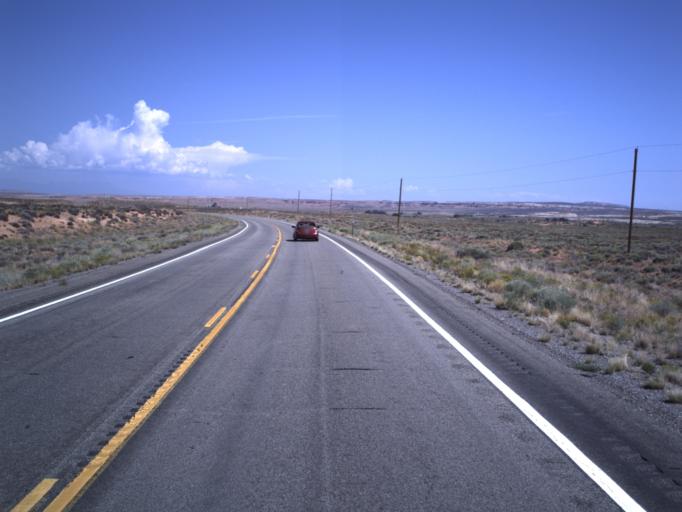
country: US
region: Utah
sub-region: San Juan County
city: Blanding
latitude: 37.0747
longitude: -109.5491
